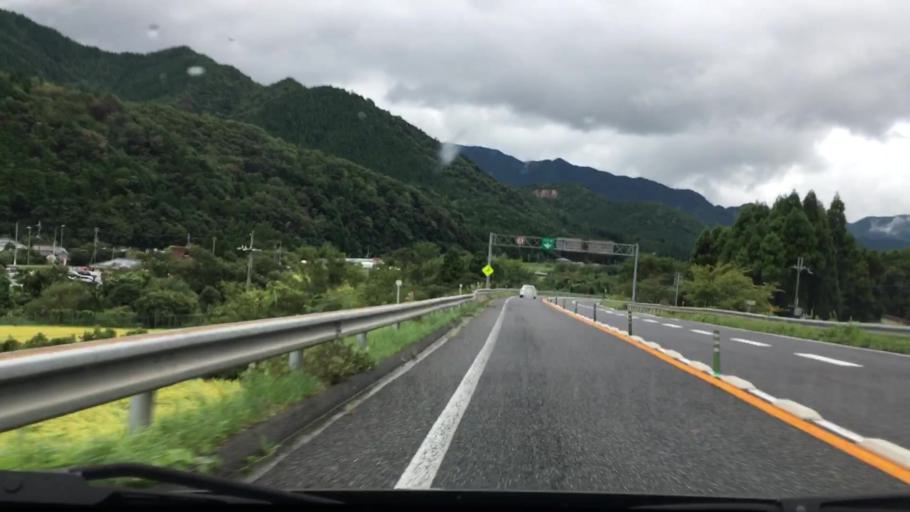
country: JP
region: Hyogo
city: Nishiwaki
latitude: 35.0926
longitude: 134.7763
